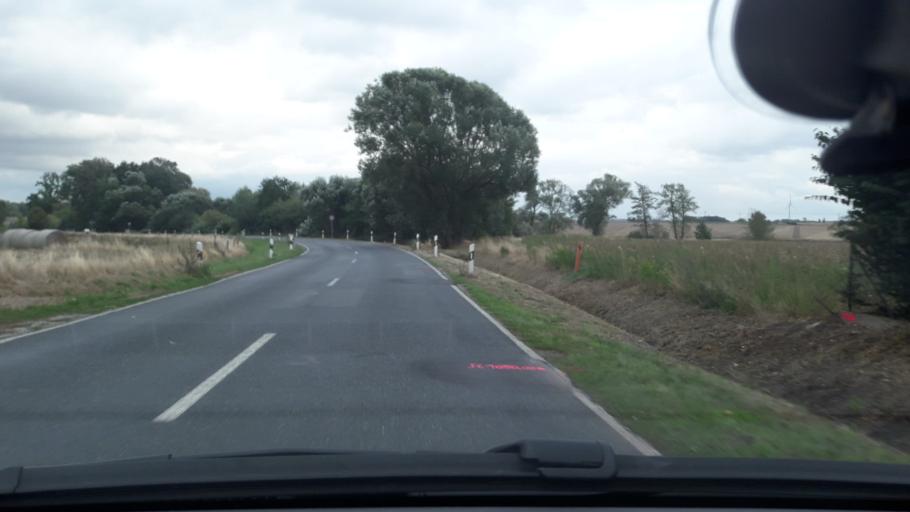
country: DE
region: Lower Saxony
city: Velpke
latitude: 52.4040
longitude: 10.9501
